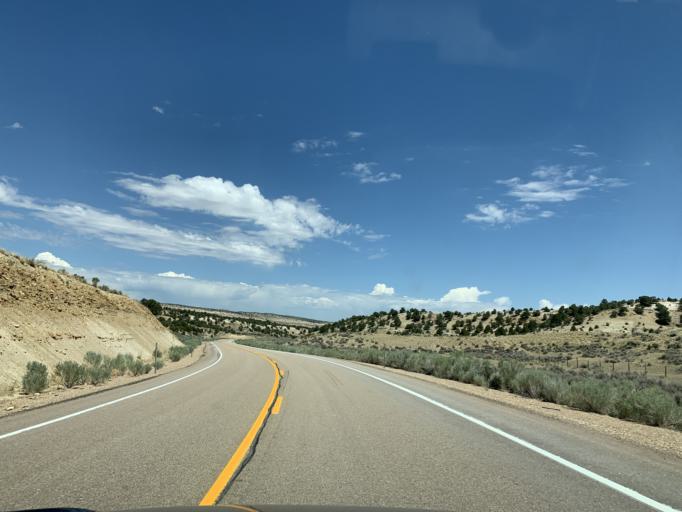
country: US
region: Utah
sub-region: Duchesne County
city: Duchesne
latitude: 39.9073
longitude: -110.2307
